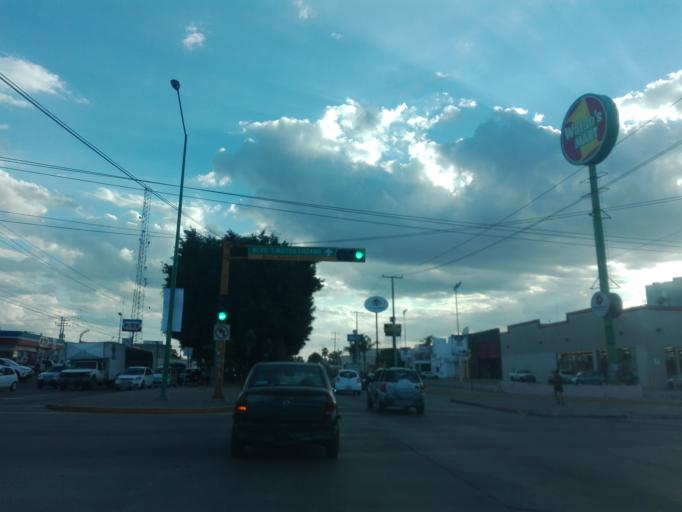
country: MX
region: Guanajuato
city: Leon
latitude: 21.1068
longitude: -101.6579
